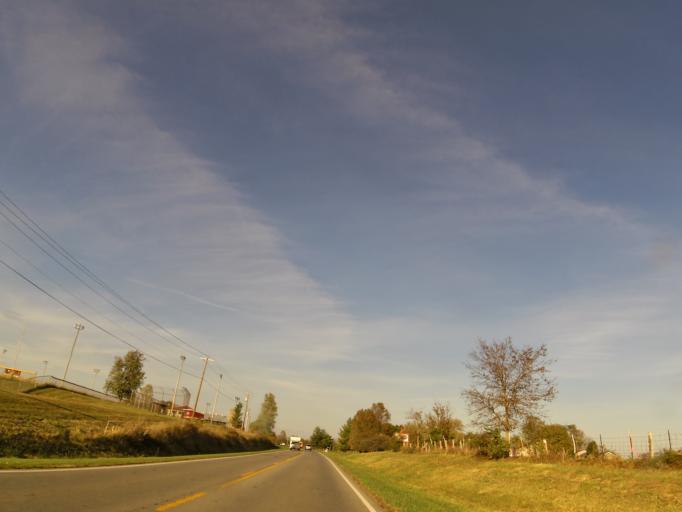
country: US
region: Kentucky
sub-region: Garrard County
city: Lancaster
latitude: 37.5909
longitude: -84.5981
